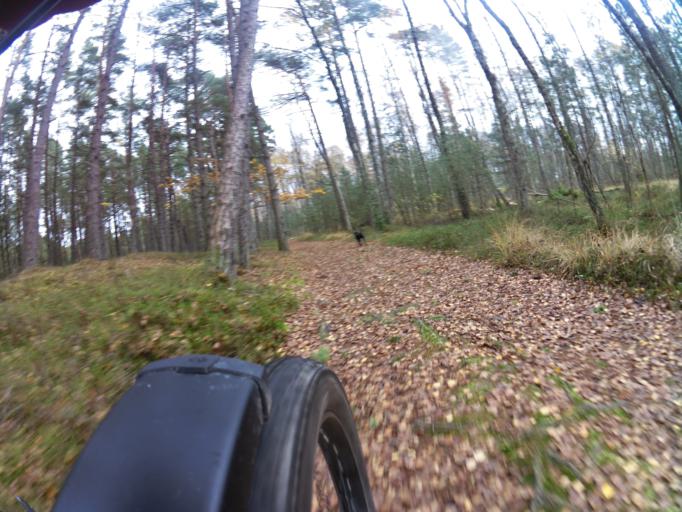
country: PL
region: Pomeranian Voivodeship
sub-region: Powiat leborski
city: Leba
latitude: 54.7668
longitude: 17.6014
